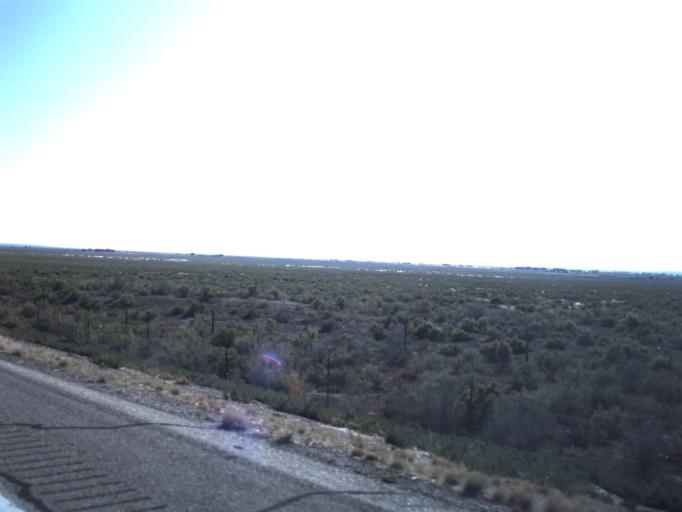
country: US
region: Utah
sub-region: Millard County
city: Delta
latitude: 39.3507
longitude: -112.4967
